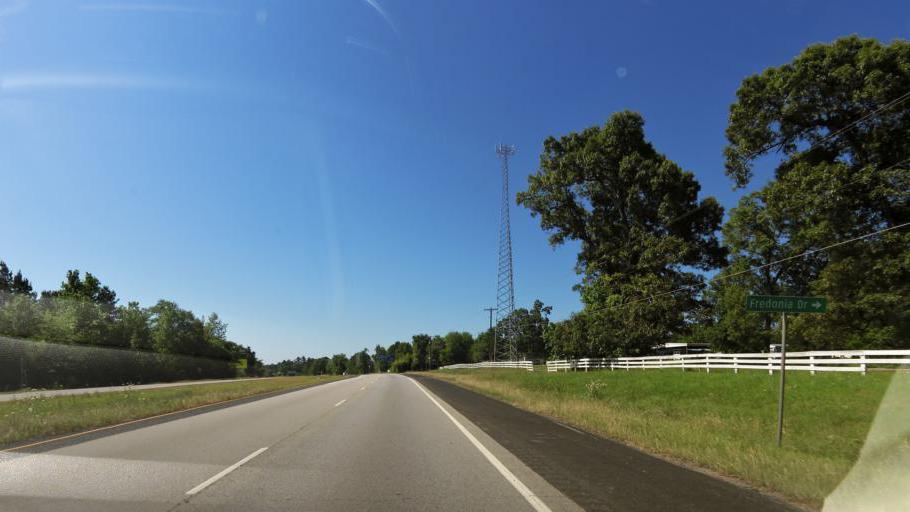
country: US
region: Texas
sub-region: Angelina County
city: Redland
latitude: 31.4323
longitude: -94.7270
